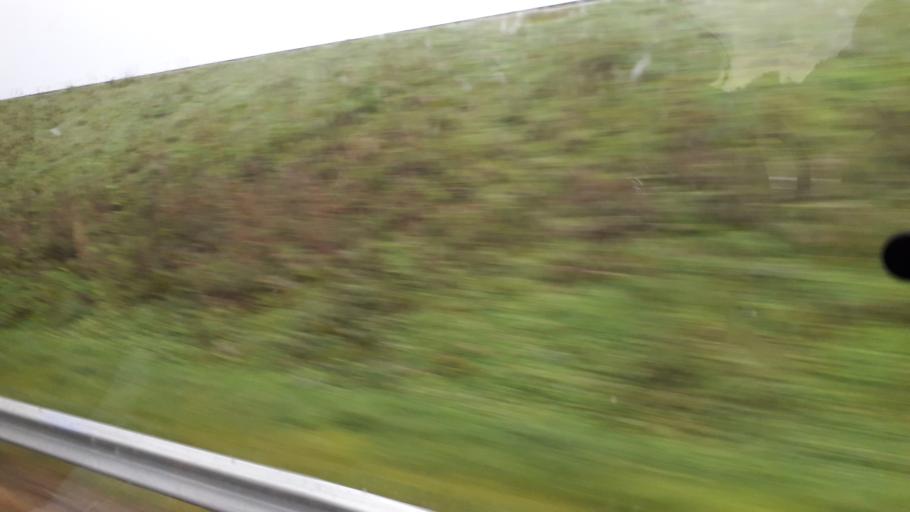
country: IE
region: Connaught
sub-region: County Galway
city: Athenry
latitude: 53.2937
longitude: -8.8085
